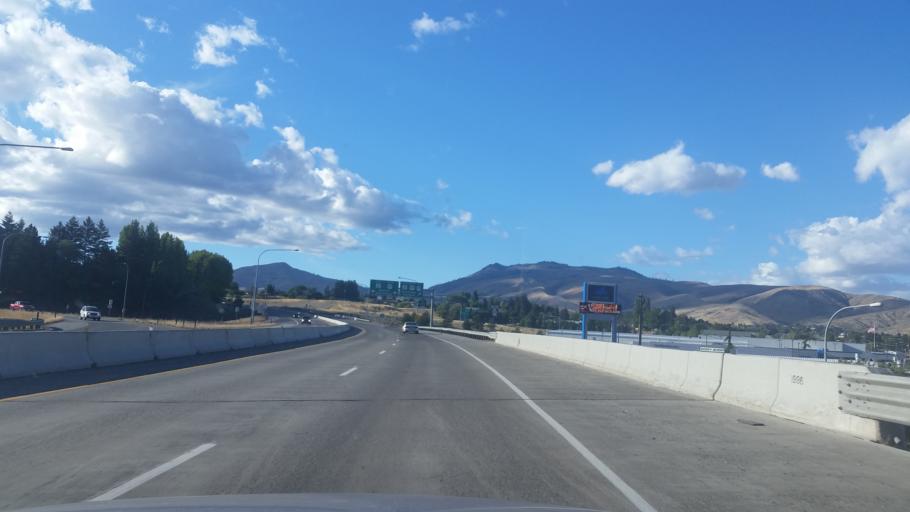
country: US
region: Washington
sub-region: Chelan County
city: Sunnyslope
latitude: 47.4651
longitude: -120.3367
